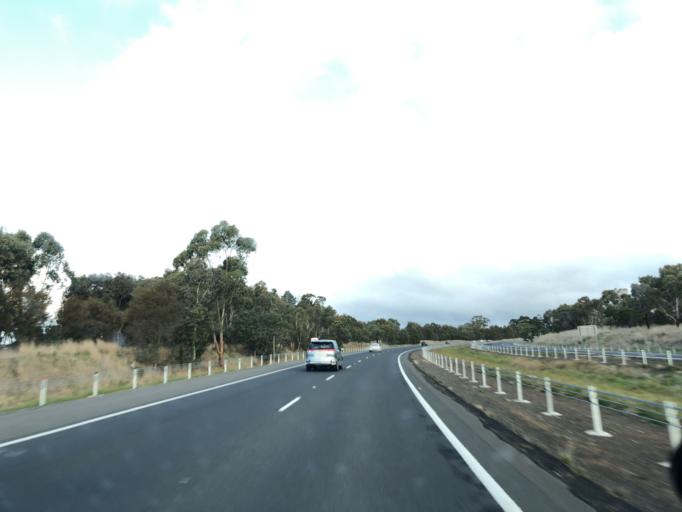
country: AU
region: Victoria
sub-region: Mount Alexander
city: Castlemaine
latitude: -37.2473
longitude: 144.4717
